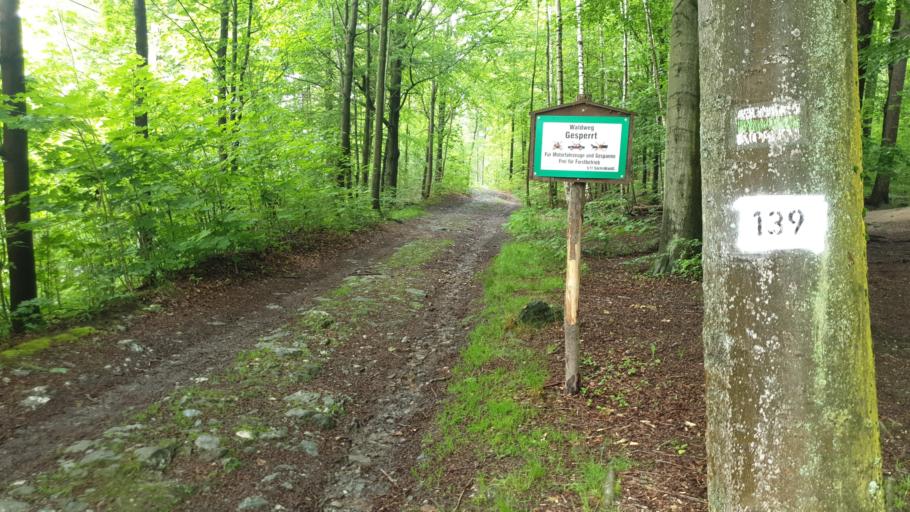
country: DE
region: Saxony
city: Chemnitz
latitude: 50.7844
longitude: 12.9693
